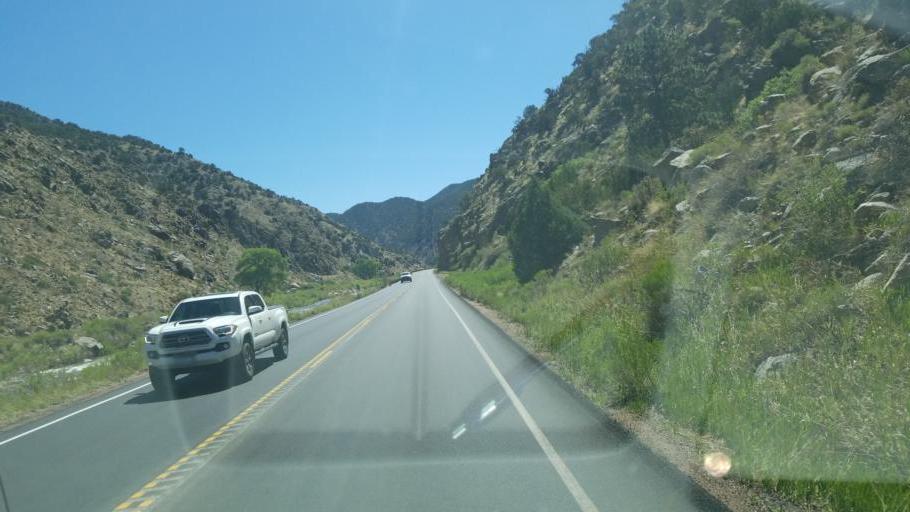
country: US
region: Colorado
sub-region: Fremont County
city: Canon City
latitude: 38.4578
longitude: -105.4818
